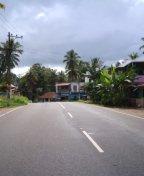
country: IN
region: Kerala
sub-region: Thrissur District
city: Trichur
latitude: 10.5255
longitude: 76.3564
